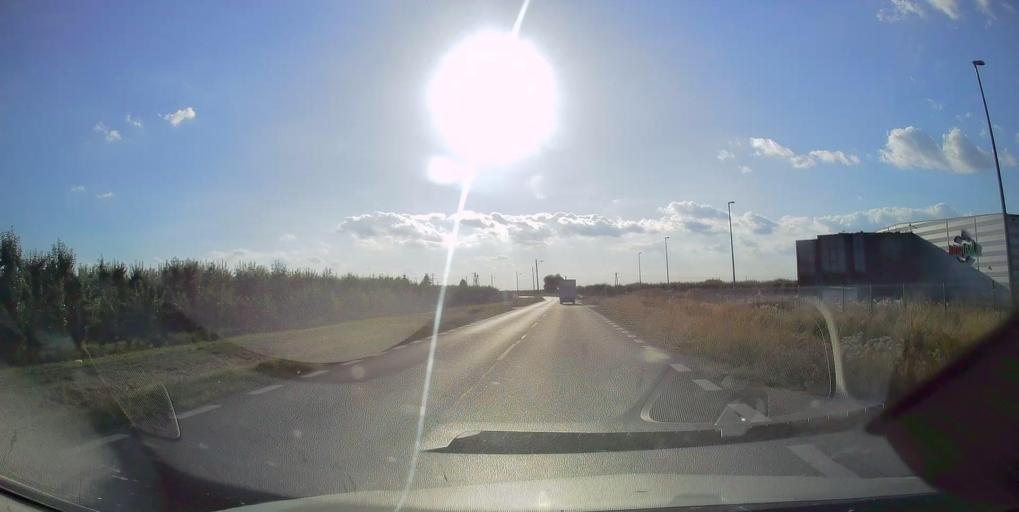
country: PL
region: Lodz Voivodeship
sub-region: Powiat rawski
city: Biala Rawska
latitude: 51.8072
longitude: 20.5675
